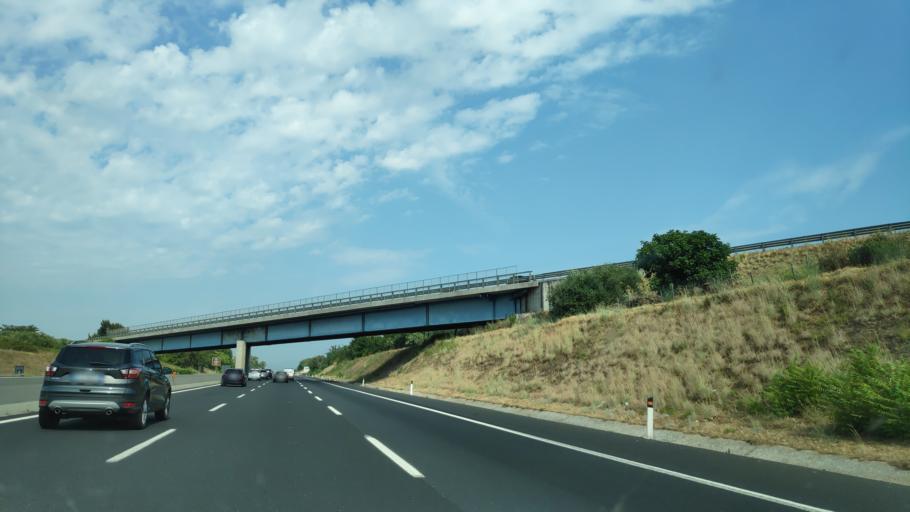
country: IT
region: Campania
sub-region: Provincia di Caserta
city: San Prisco
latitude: 41.0928
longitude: 14.2776
